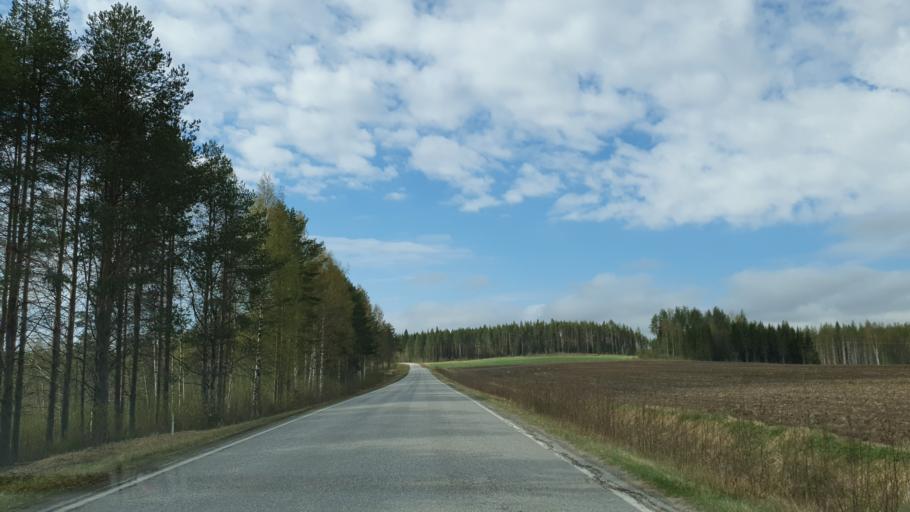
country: FI
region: Kainuu
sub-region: Kehys-Kainuu
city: Kuhmo
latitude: 64.1193
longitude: 29.6951
